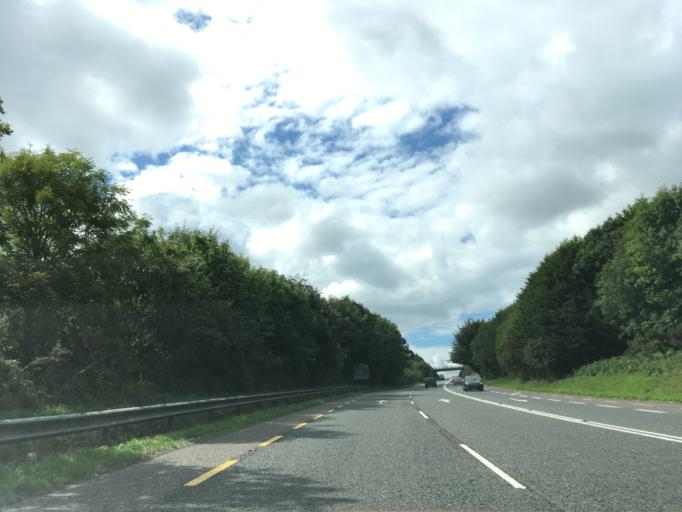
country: IE
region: Munster
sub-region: County Cork
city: Carrigaline
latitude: 51.8696
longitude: -8.4128
